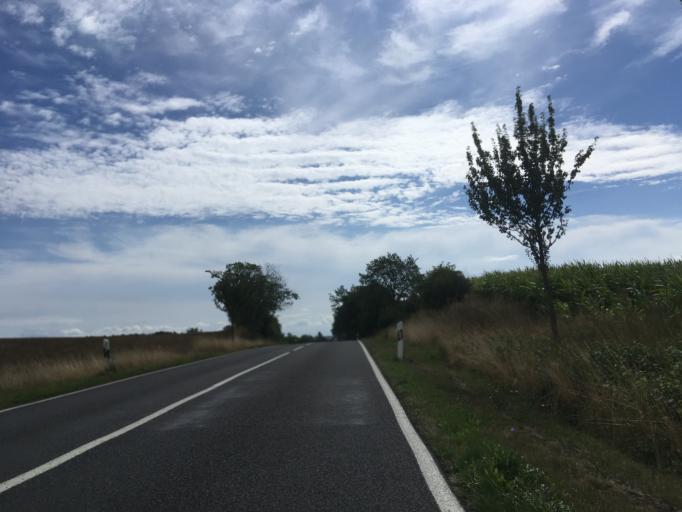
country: DE
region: Brandenburg
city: Gerswalde
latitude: 53.1774
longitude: 13.7429
